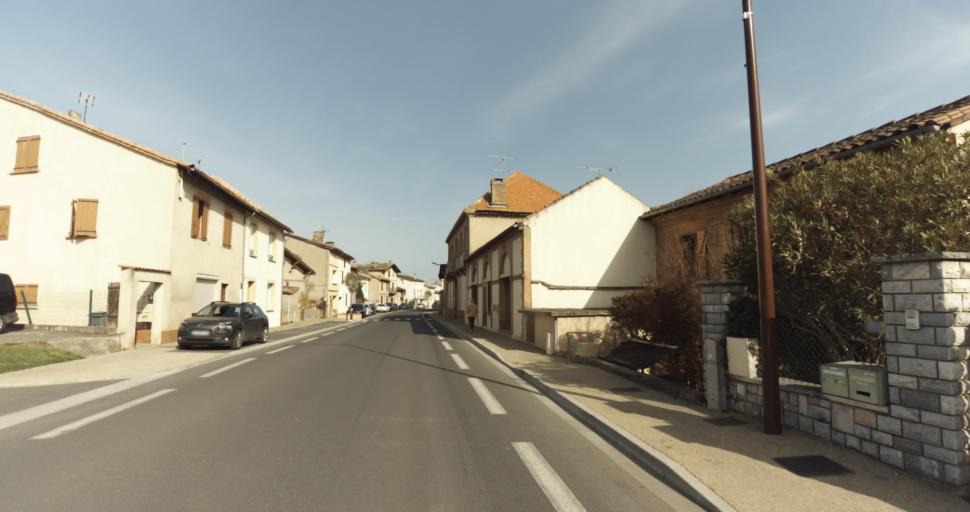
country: FR
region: Midi-Pyrenees
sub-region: Departement du Tarn
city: Saint-Sulpice-la-Pointe
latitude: 43.7706
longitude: 1.6889
